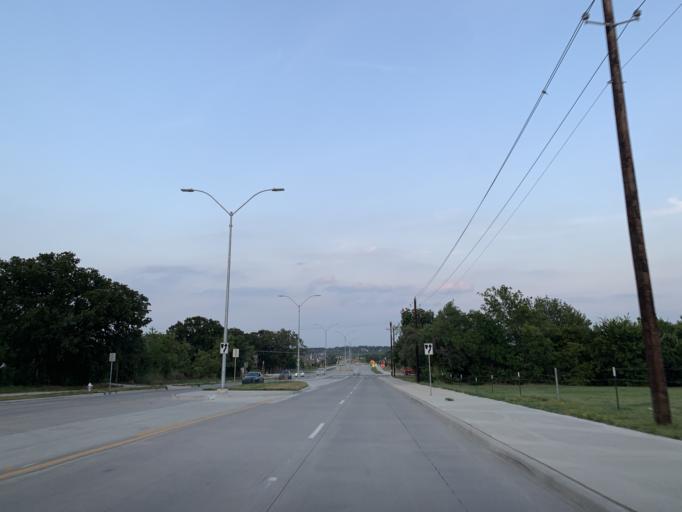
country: US
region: Texas
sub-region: Tarrant County
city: Keller
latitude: 32.9554
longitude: -97.2712
